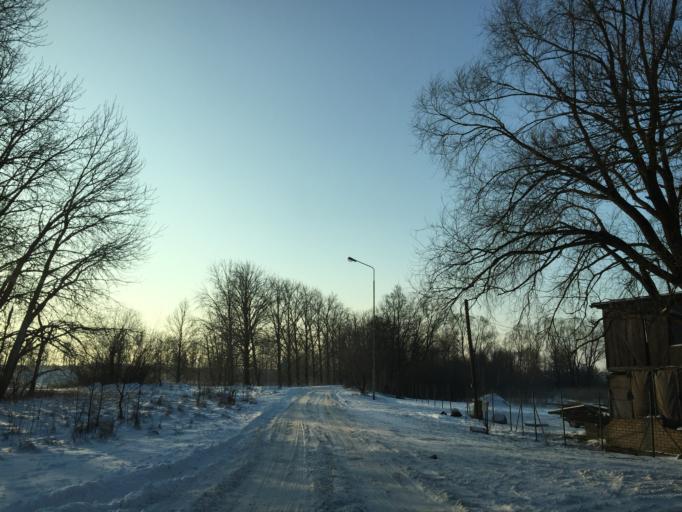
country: LV
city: Tireli
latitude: 56.9359
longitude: 23.6078
